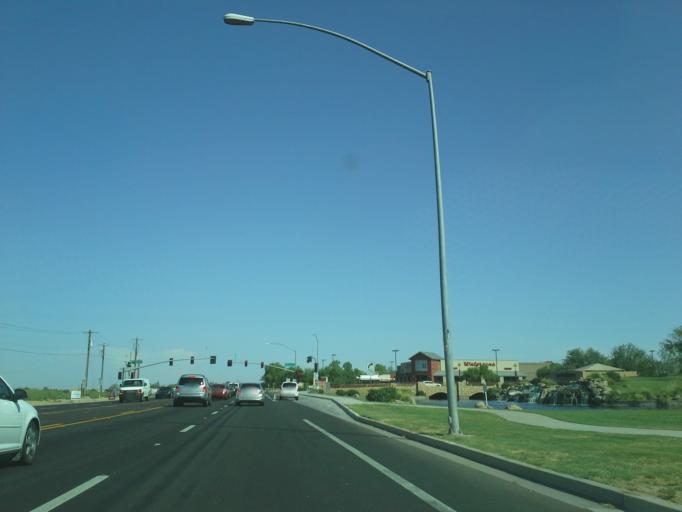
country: US
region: Arizona
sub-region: Maricopa County
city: Queen Creek
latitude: 33.1915
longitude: -111.6012
